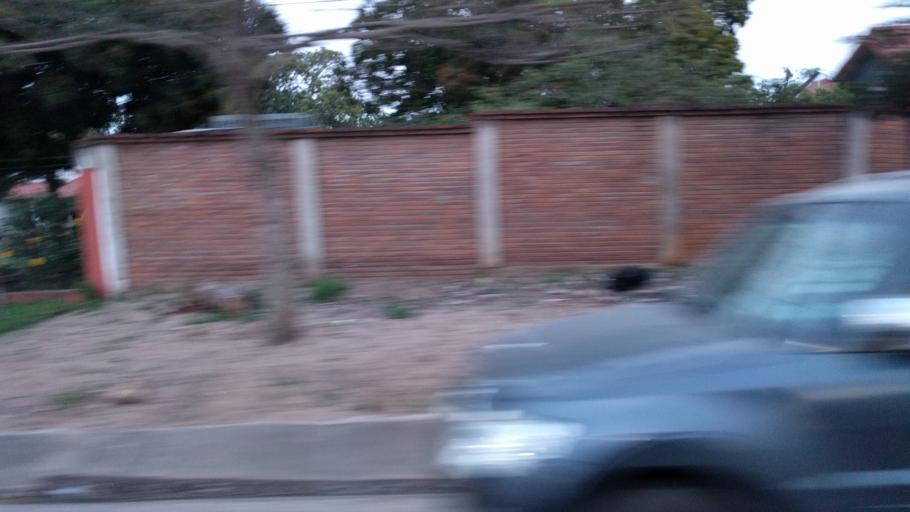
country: BO
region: Santa Cruz
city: Santa Rita
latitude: -17.8833
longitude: -63.2916
